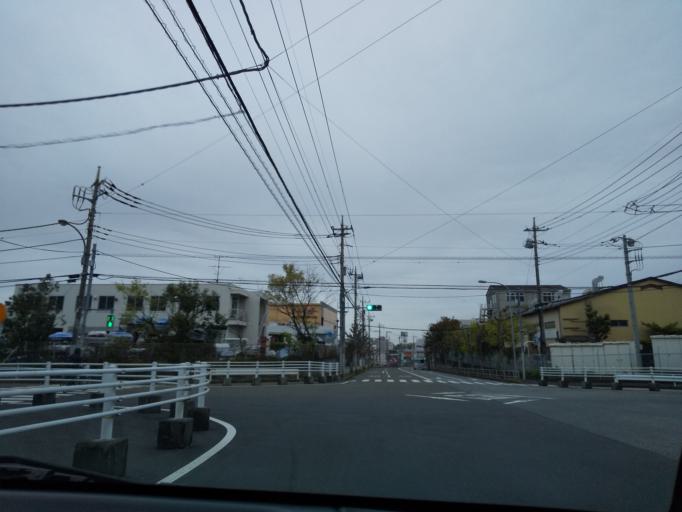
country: JP
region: Tokyo
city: Hino
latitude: 35.6748
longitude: 139.3703
